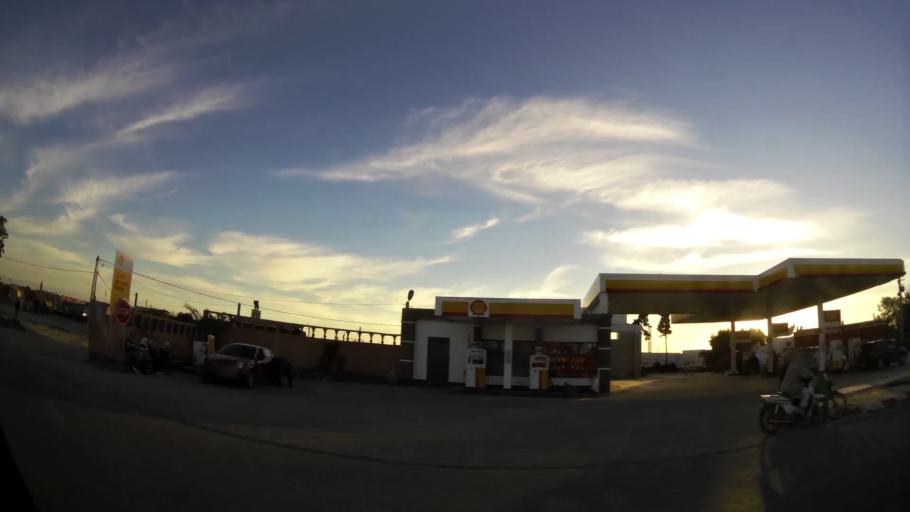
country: MA
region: Marrakech-Tensift-Al Haouz
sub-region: Marrakech
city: Marrakesh
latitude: 31.7591
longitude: -8.1142
